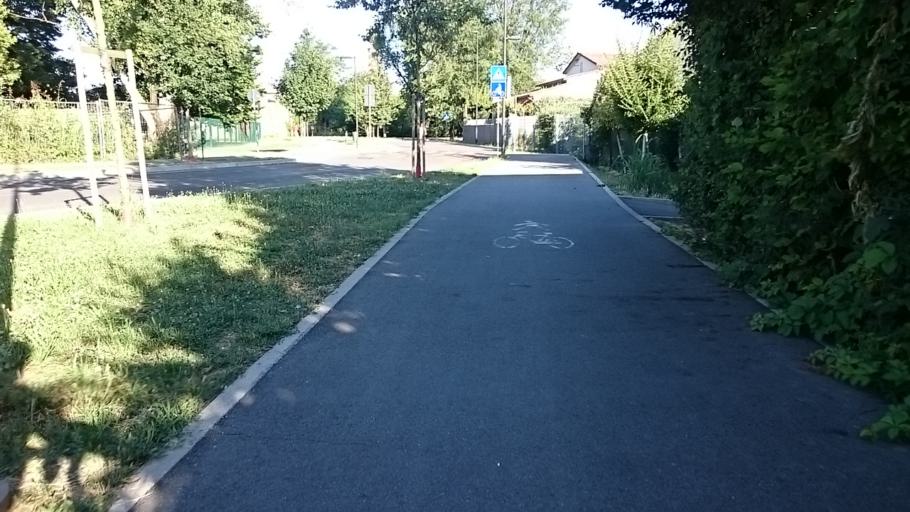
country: IT
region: Veneto
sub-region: Provincia di Padova
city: Padova
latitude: 45.4208
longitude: 11.8913
